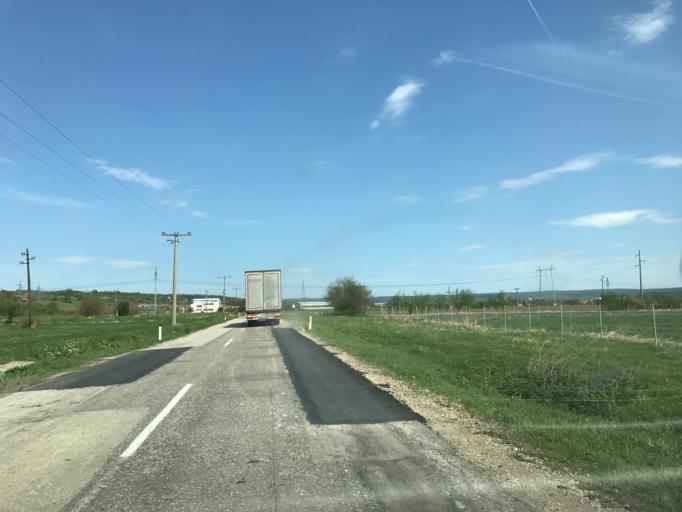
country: RS
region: Central Serbia
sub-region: Zajecarski Okrug
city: Zajecar
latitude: 43.9039
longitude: 22.2301
